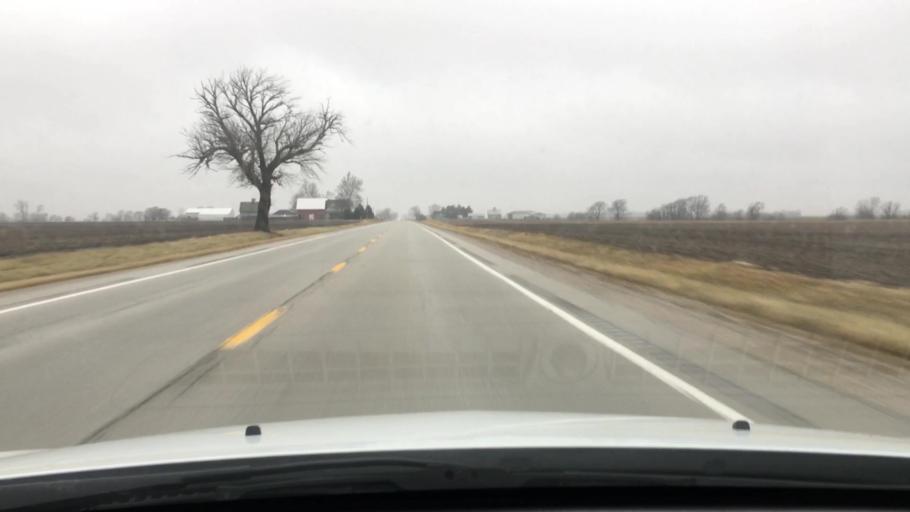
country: US
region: Illinois
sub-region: Livingston County
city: Pontiac
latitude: 40.8727
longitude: -88.7363
